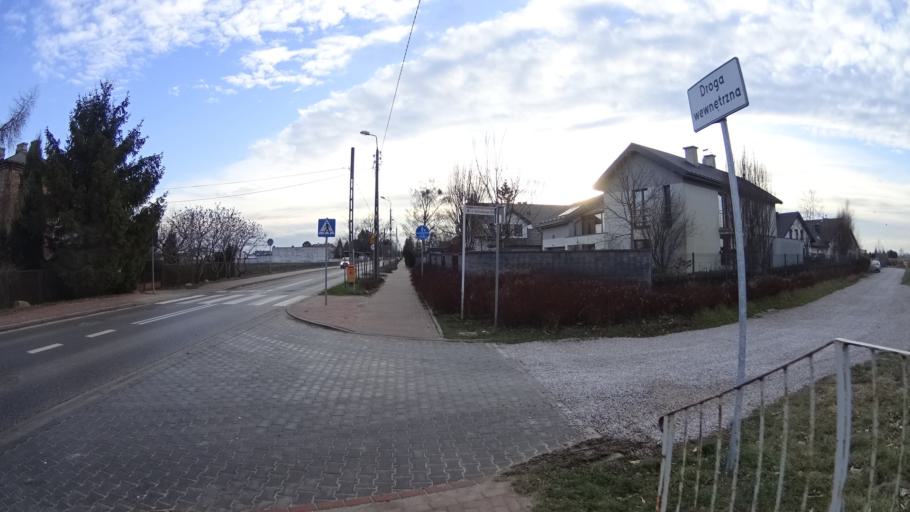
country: PL
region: Masovian Voivodeship
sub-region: Powiat warszawski zachodni
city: Ozarow Mazowiecki
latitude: 52.2270
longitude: 20.8021
